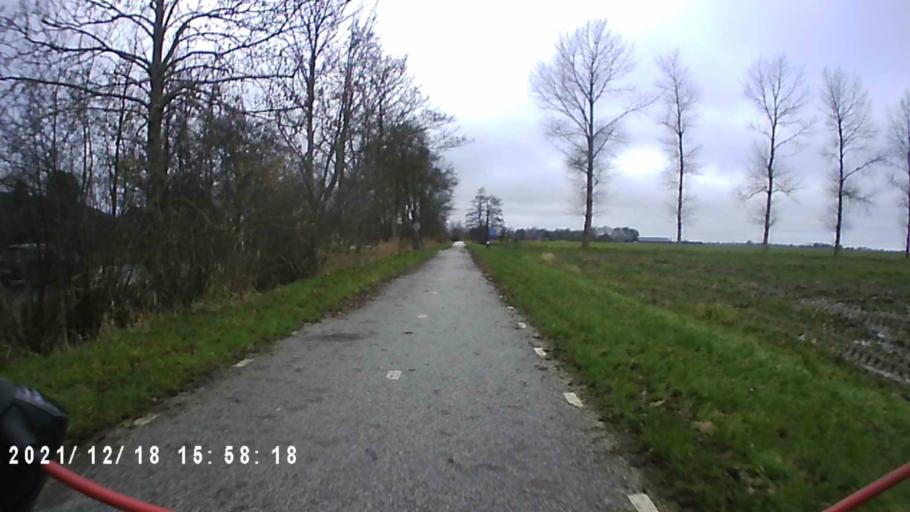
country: NL
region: Friesland
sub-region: Gemeente Dongeradeel
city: Anjum
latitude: 53.3367
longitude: 6.0930
